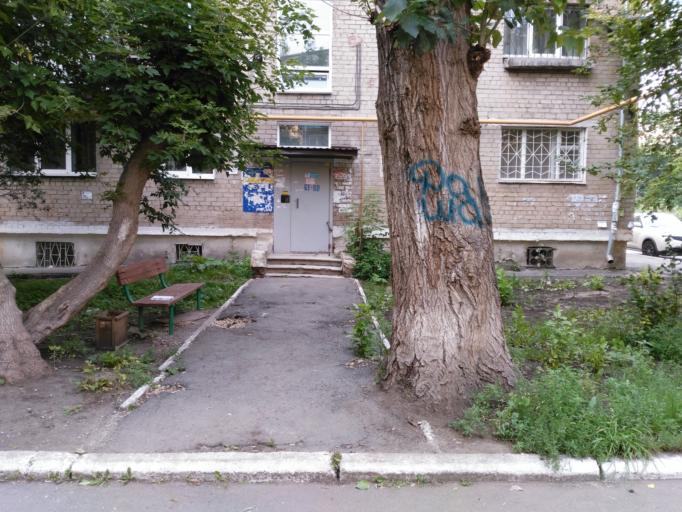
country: RU
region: Chelyabinsk
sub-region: Gorod Chelyabinsk
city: Chelyabinsk
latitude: 55.1547
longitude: 61.3955
